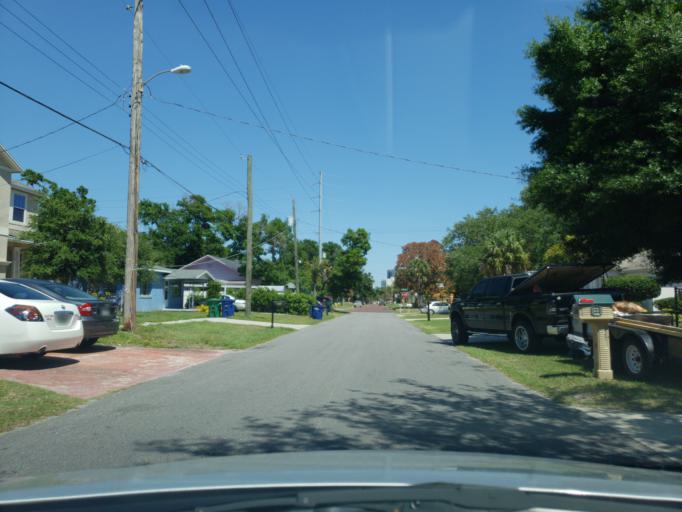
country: US
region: Florida
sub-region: Hillsborough County
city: Tampa
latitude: 27.9527
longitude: -82.4735
